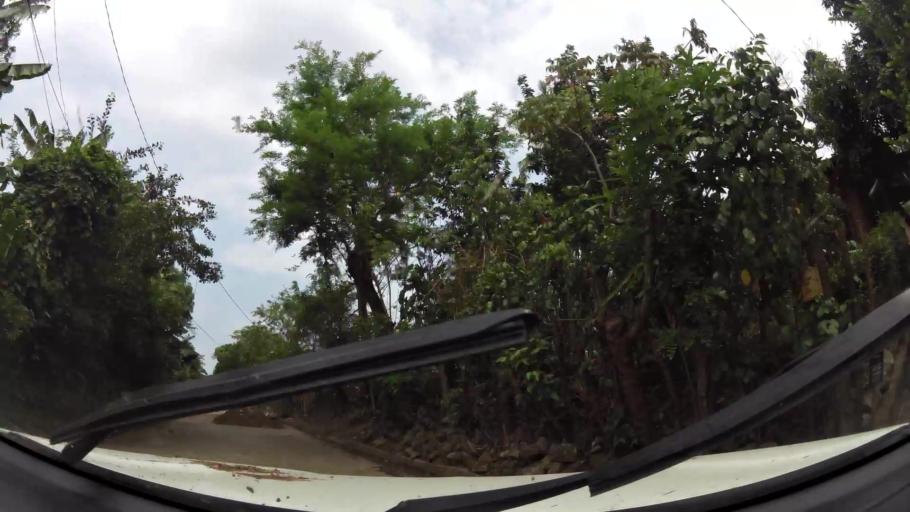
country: NI
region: Granada
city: Diriomo
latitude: 11.8721
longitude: -86.0512
